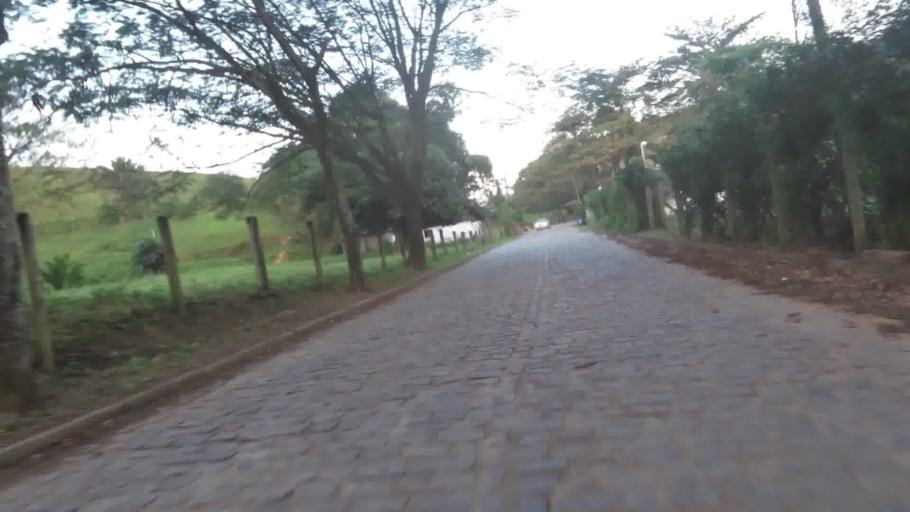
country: BR
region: Espirito Santo
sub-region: Alfredo Chaves
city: Alfredo Chaves
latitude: -20.6496
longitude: -40.6432
